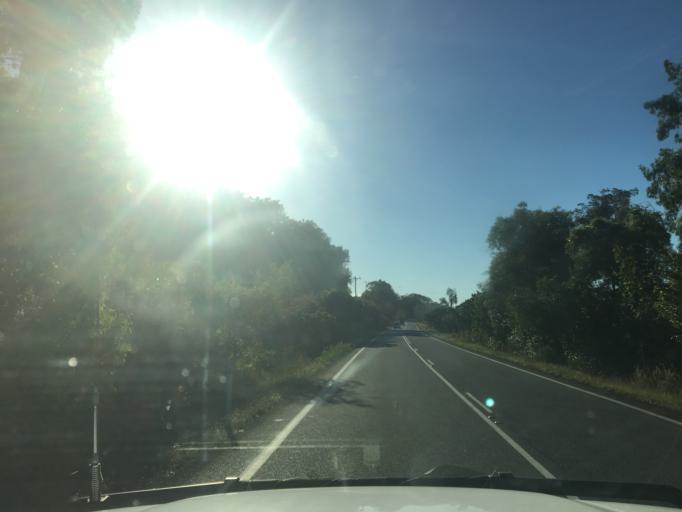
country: AU
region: Queensland
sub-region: Cairns
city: Port Douglas
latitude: -16.5671
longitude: 145.5031
